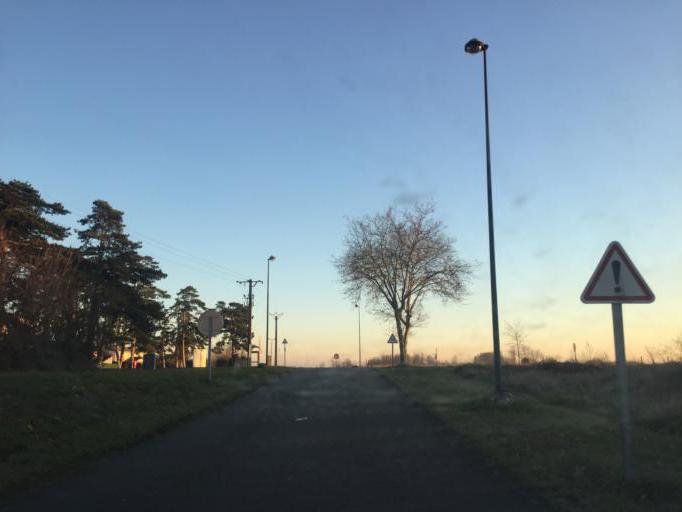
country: FR
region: Rhone-Alpes
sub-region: Departement de l'Ain
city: Beligneux
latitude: 45.8534
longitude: 5.1430
